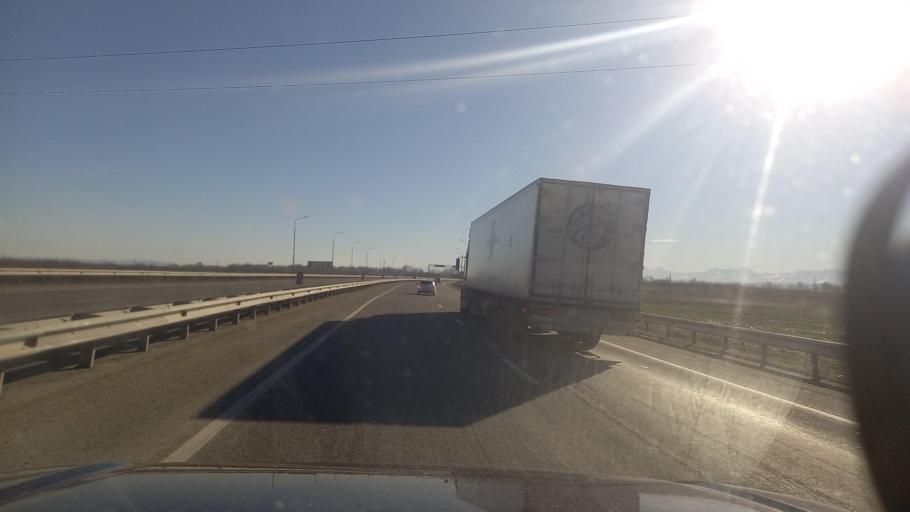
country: RU
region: Kabardino-Balkariya
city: Germenchik
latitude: 43.5720
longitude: 43.7130
